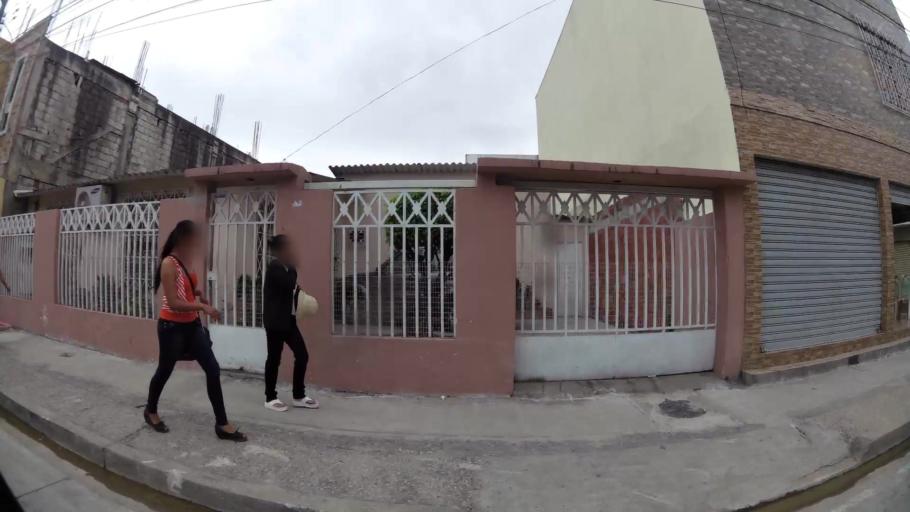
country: EC
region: Guayas
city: Eloy Alfaro
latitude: -2.1413
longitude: -79.8958
